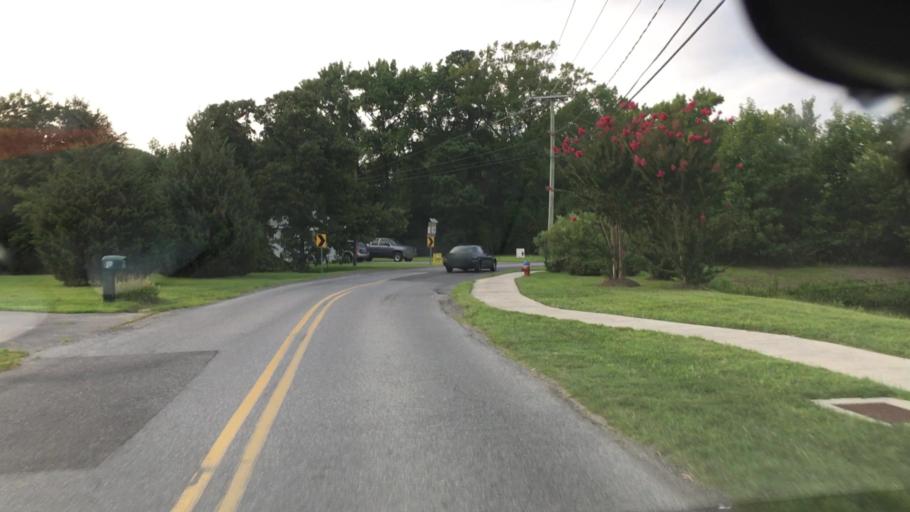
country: US
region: Delaware
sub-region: Sussex County
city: Ocean View
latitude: 38.5408
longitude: -75.0959
